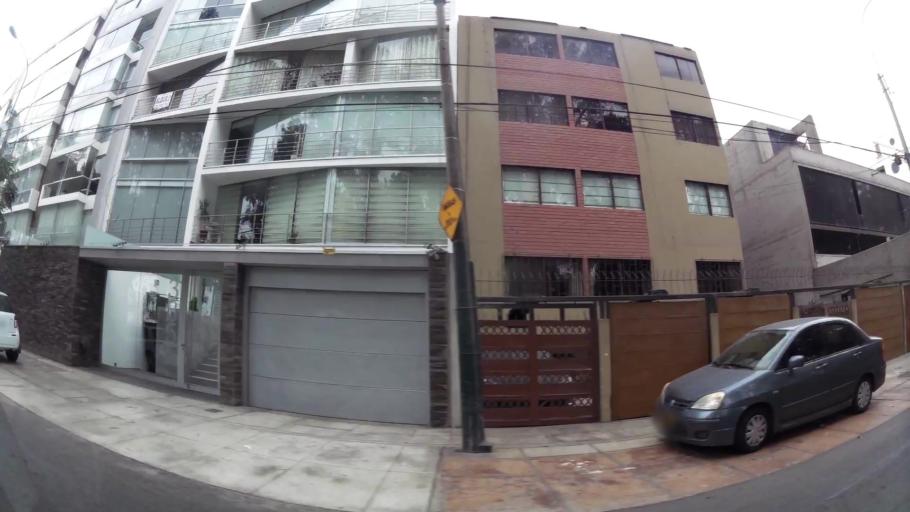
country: PE
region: Lima
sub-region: Lima
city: San Luis
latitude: -12.1036
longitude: -77.0135
